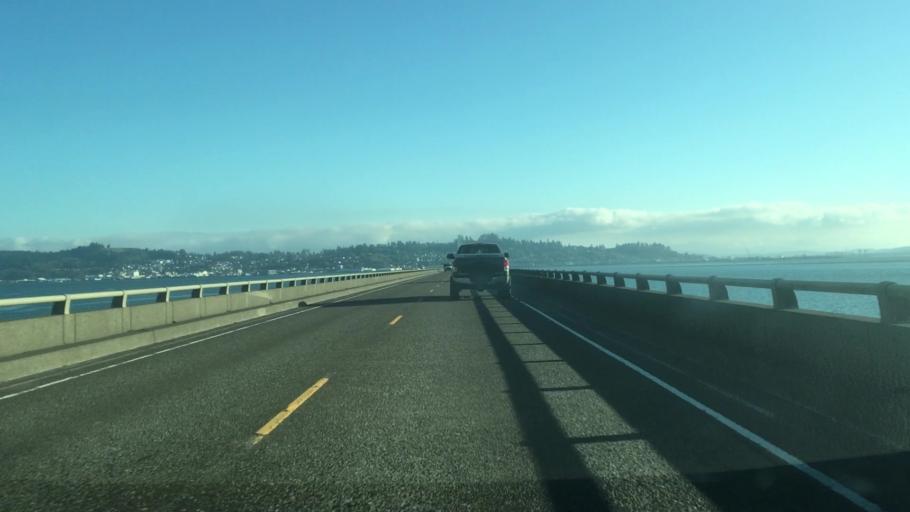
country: US
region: Oregon
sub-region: Clatsop County
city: Astoria
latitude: 46.2188
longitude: -123.8638
